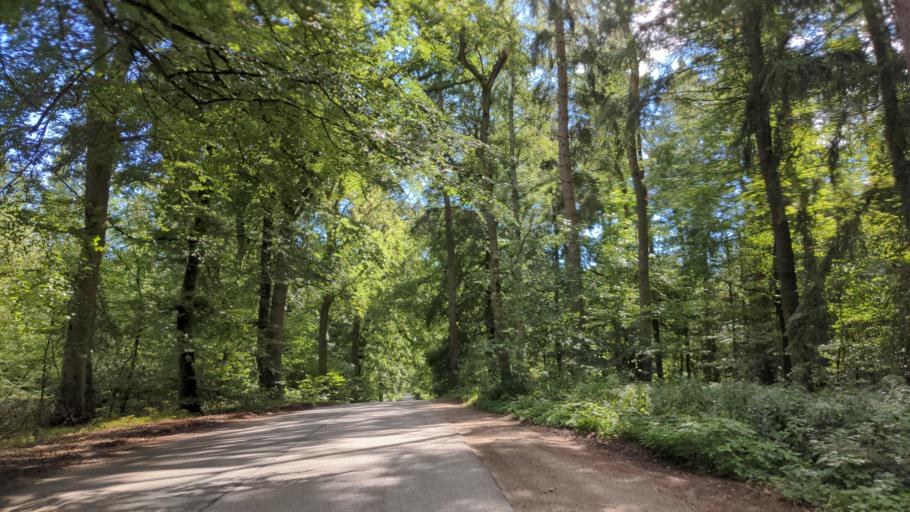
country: DE
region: Schleswig-Holstein
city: Kasseedorf
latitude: 54.1539
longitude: 10.6870
